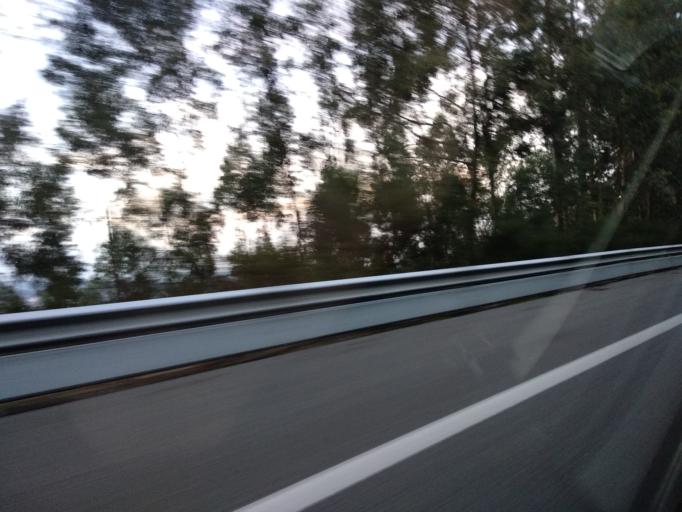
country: PT
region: Braga
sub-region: Braga
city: Oliveira
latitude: 41.4627
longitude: -8.4751
